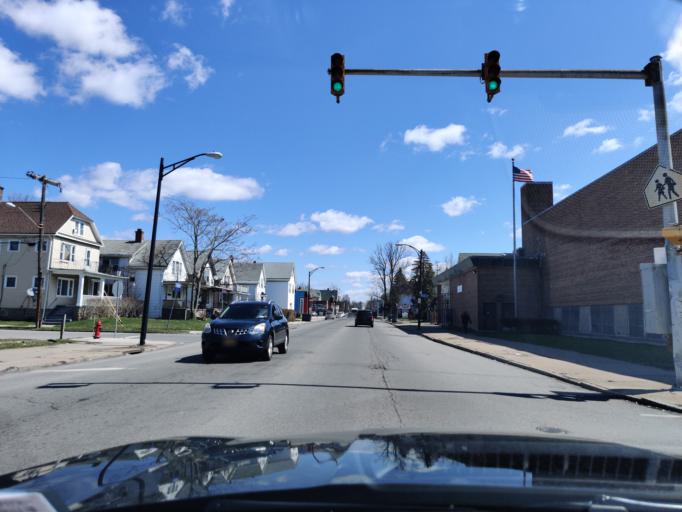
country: US
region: New York
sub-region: Erie County
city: Sloan
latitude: 42.9227
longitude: -78.8050
